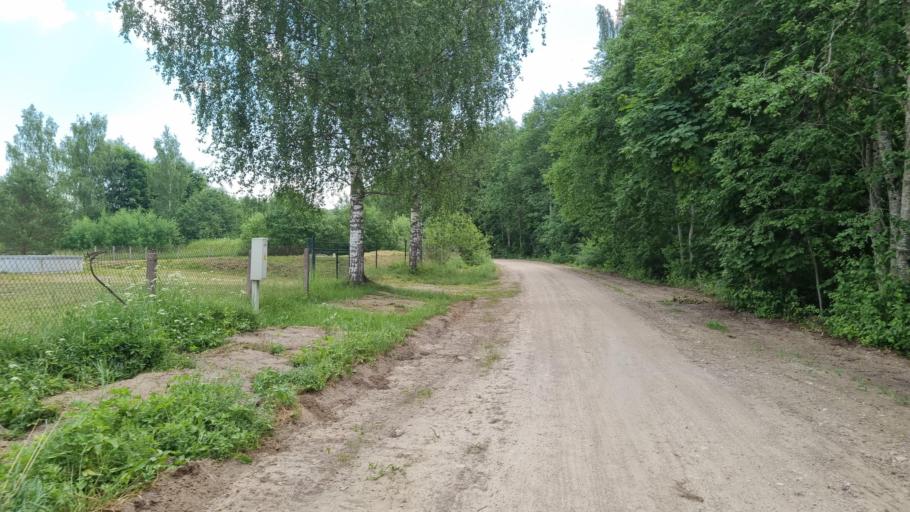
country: LV
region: Talsu Rajons
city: Stende
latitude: 57.0690
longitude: 22.2803
